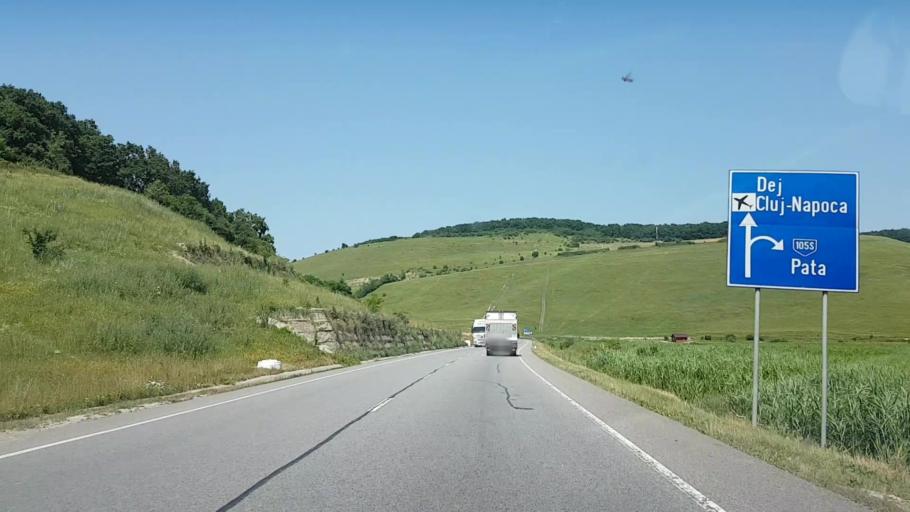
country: RO
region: Cluj
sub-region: Comuna Apahida
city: Dezmir
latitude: 46.7411
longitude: 23.7097
